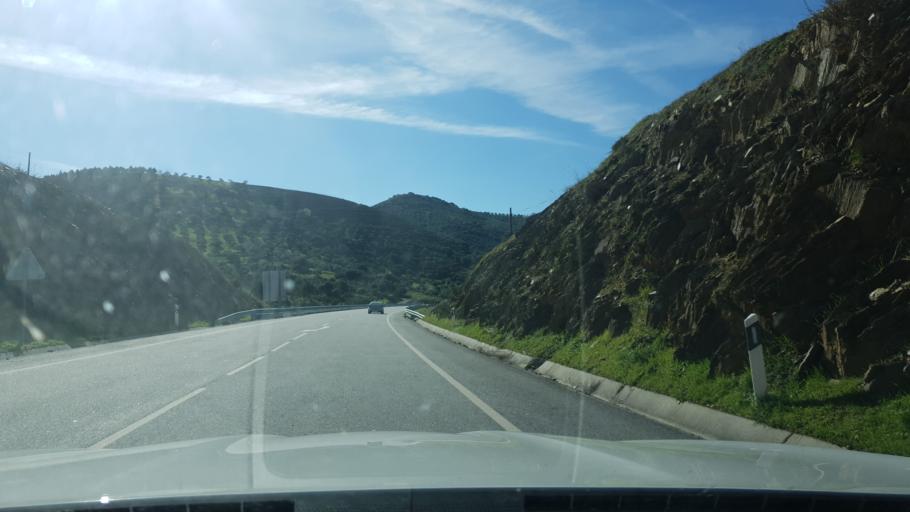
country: PT
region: Braganca
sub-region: Torre de Moncorvo
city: Torre de Moncorvo
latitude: 41.2074
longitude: -7.0814
